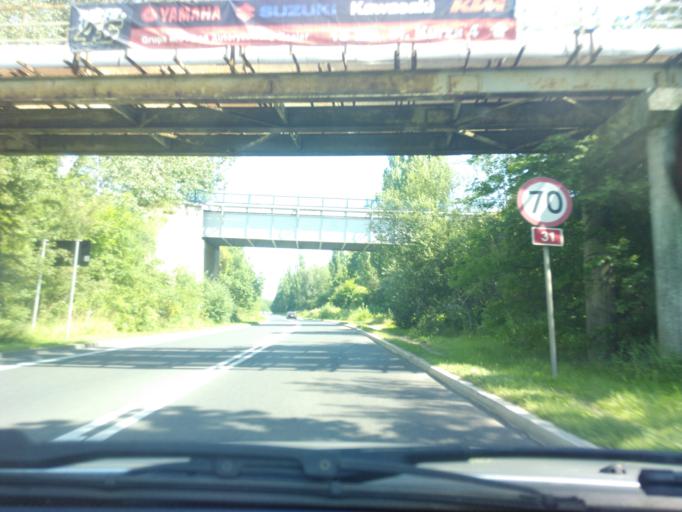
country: PL
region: West Pomeranian Voivodeship
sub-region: Powiat policki
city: Przeclaw
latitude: 53.3872
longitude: 14.5172
